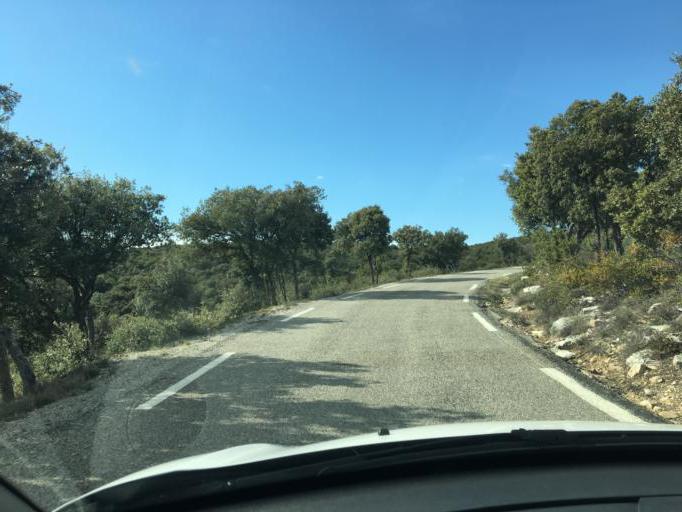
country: FR
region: Provence-Alpes-Cote d'Azur
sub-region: Departement du Vaucluse
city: Saint-Saturnin-les-Apt
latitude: 43.9407
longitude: 5.4492
